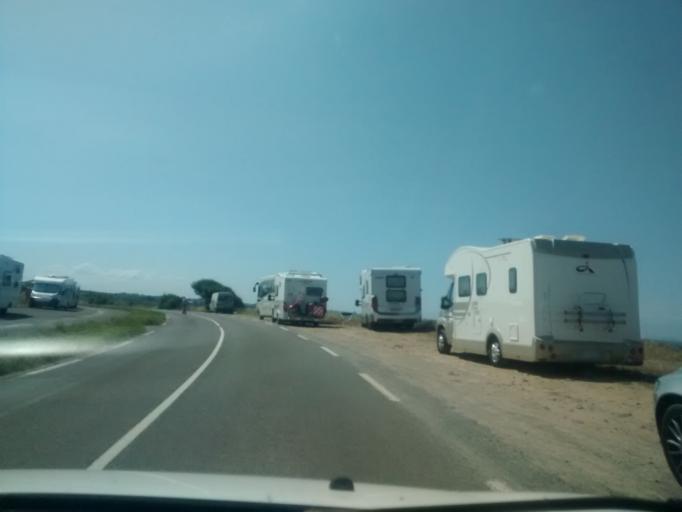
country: FR
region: Brittany
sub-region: Departement d'Ille-et-Vilaine
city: Cancale
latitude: 48.7053
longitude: -1.8532
